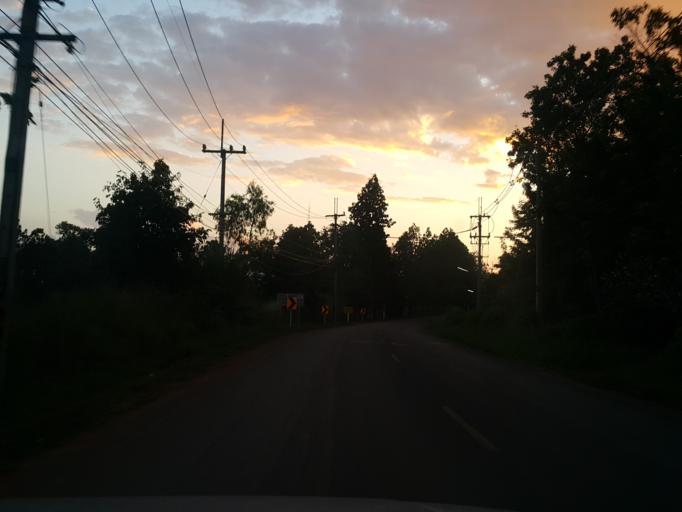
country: TH
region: Mae Hong Son
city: Khun Yuam
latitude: 18.8417
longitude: 97.9540
